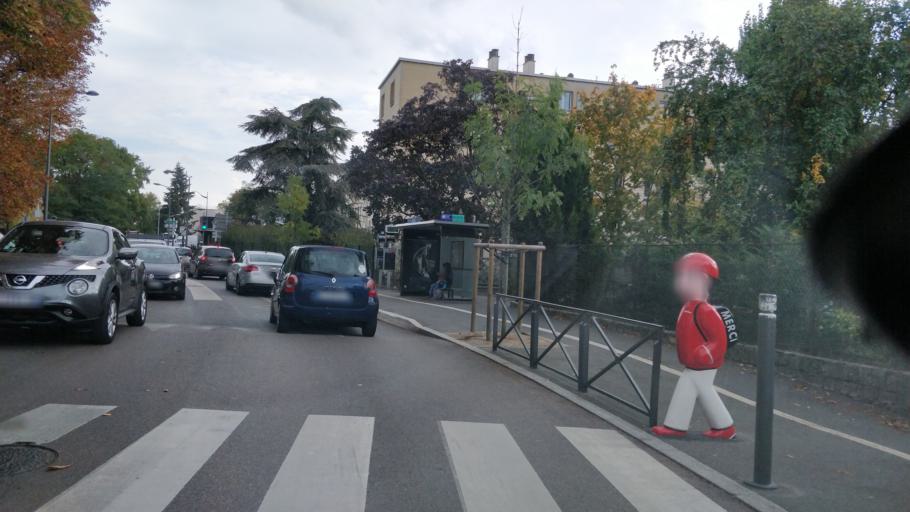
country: FR
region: Ile-de-France
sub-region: Departement de Seine-Saint-Denis
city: Clichy-sous-Bois
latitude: 48.9101
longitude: 2.5497
